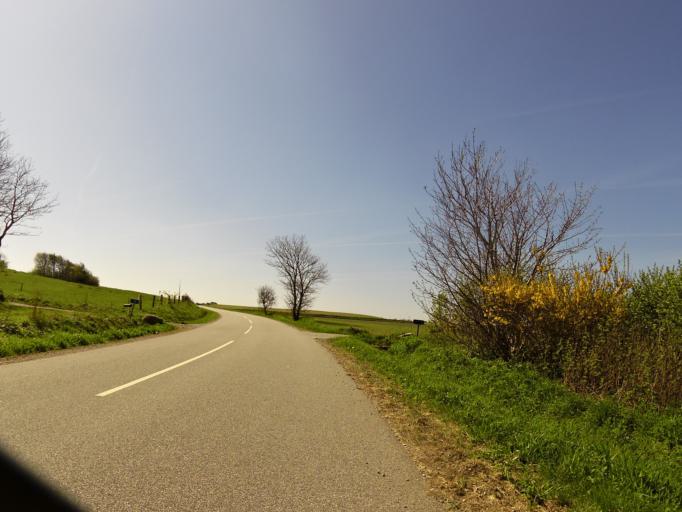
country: DK
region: Central Jutland
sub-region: Struer Kommune
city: Struer
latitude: 56.5172
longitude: 8.5951
